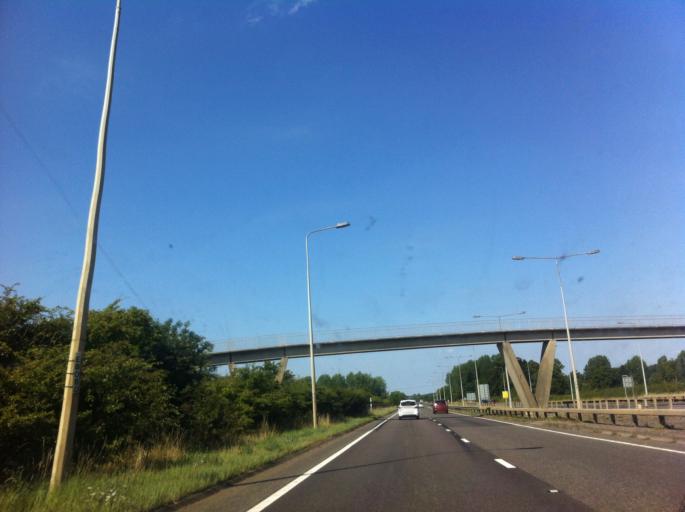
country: GB
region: England
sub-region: Northamptonshire
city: Earls Barton
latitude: 52.2543
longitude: -0.7566
